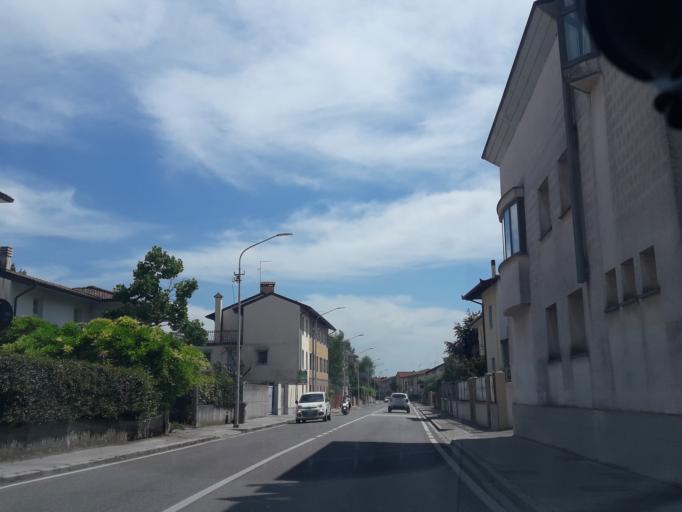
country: IT
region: Friuli Venezia Giulia
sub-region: Provincia di Udine
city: Udine
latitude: 46.0506
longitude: 13.2394
